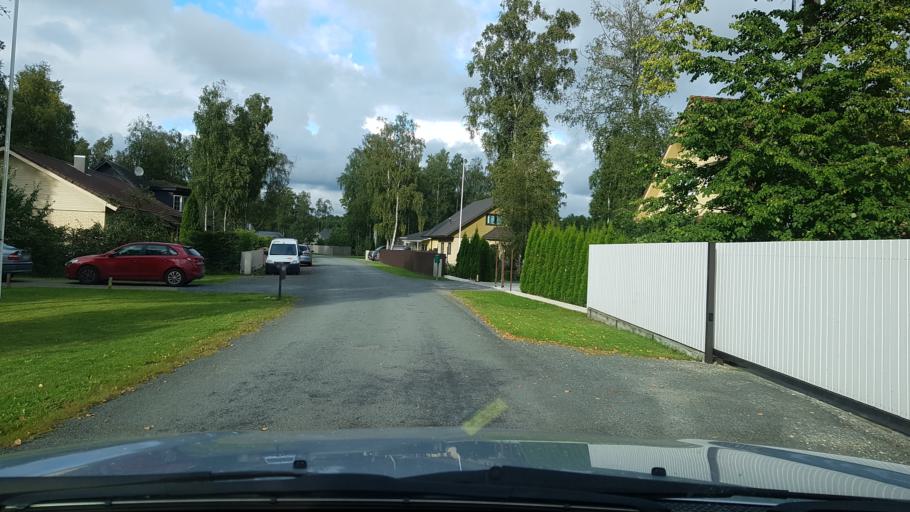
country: EE
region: Harju
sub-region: Rae vald
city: Jueri
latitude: 59.3654
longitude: 24.9142
